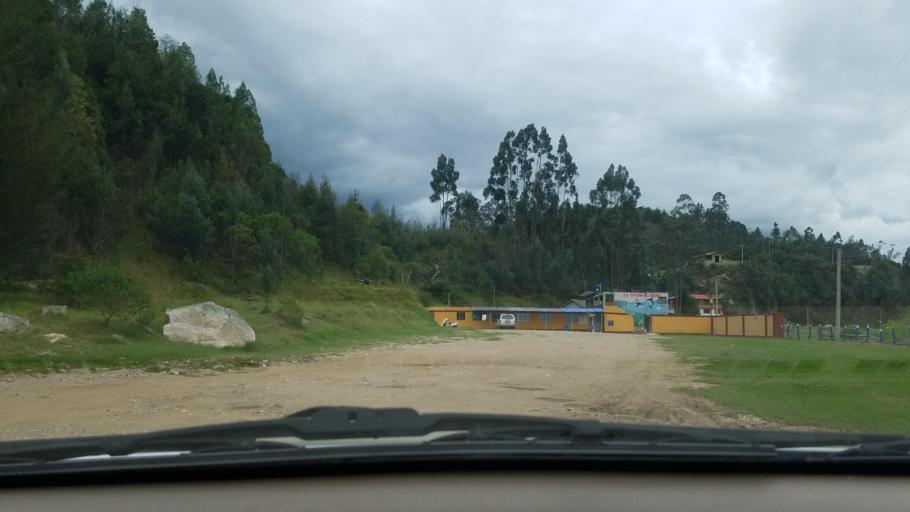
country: CO
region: Boyaca
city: Paipa
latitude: 5.7294
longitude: -73.1139
